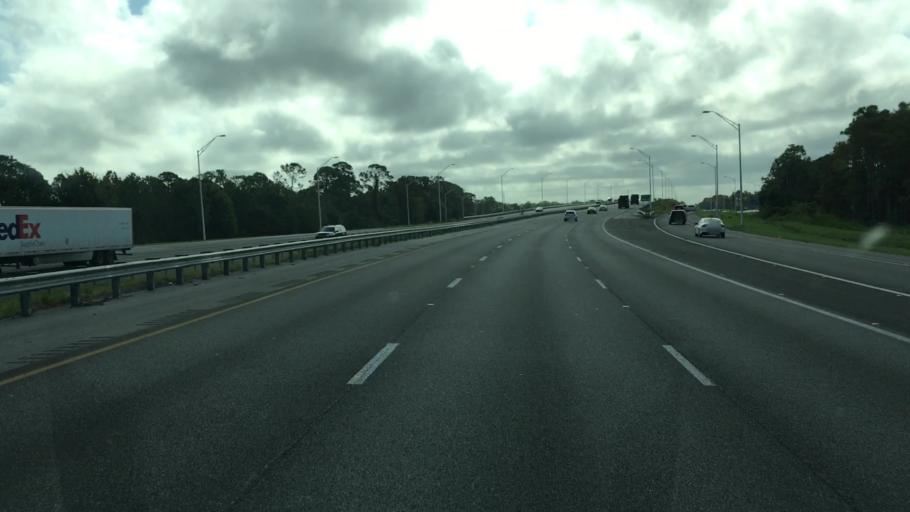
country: US
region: Florida
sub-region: Volusia County
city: Port Orange
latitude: 29.1113
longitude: -81.0316
